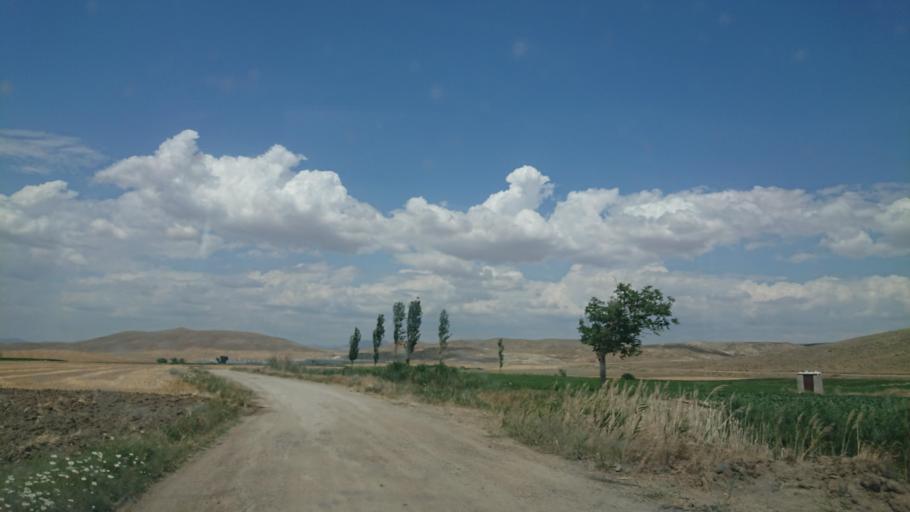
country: TR
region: Aksaray
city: Sariyahsi
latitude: 38.9867
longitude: 33.9082
